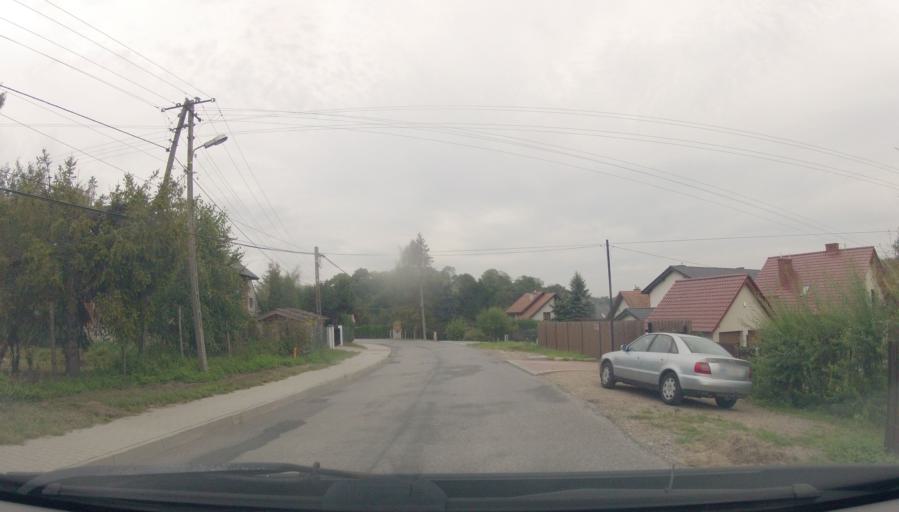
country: PL
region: Lesser Poland Voivodeship
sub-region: Powiat krakowski
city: Rzeszotary
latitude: 49.9420
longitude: 19.9910
